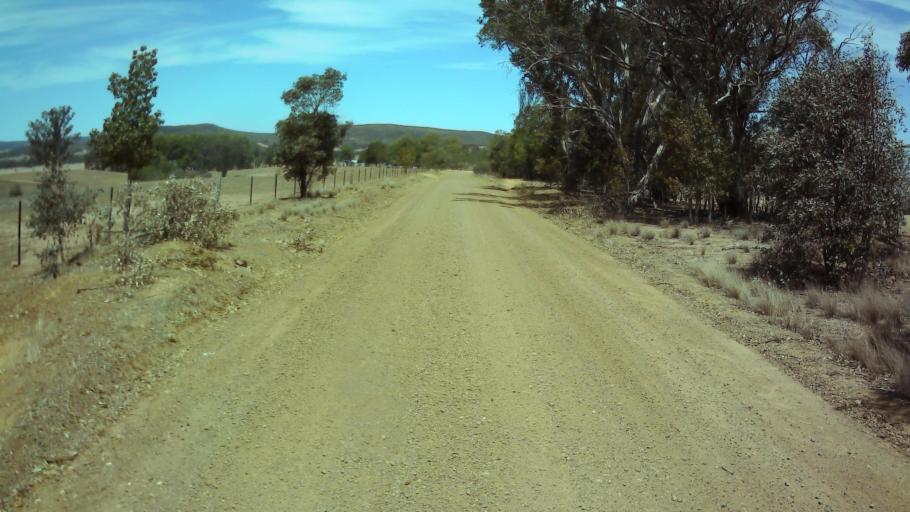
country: AU
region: New South Wales
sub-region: Weddin
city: Grenfell
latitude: -33.8276
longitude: 148.1727
